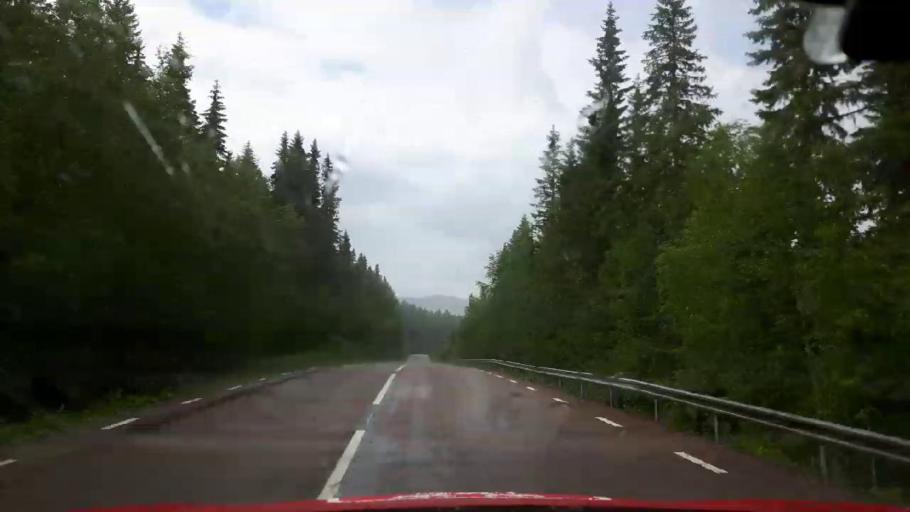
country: SE
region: Jaemtland
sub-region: Krokoms Kommun
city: Valla
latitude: 63.9540
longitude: 14.2053
